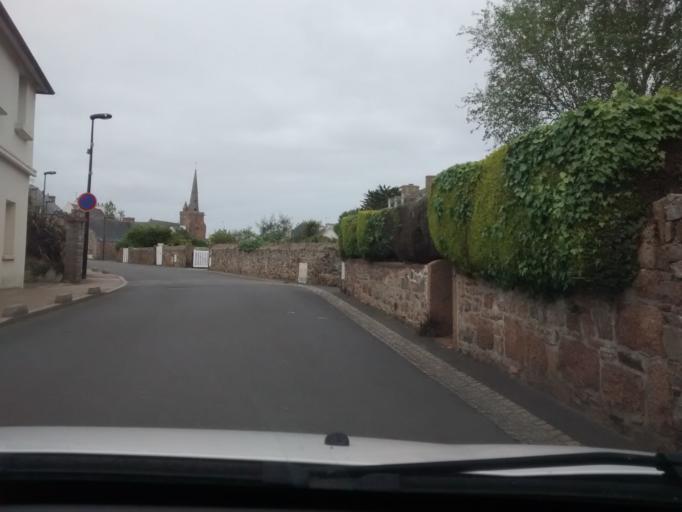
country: FR
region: Brittany
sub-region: Departement des Cotes-d'Armor
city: Tregastel
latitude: 48.8187
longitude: -3.4706
